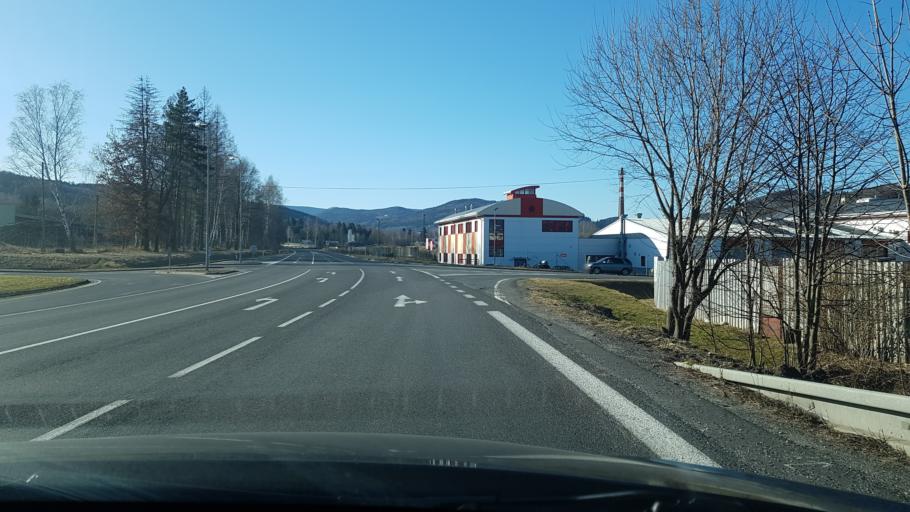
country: CZ
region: Olomoucky
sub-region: Okres Jesenik
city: Jesenik
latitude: 50.2208
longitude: 17.1899
